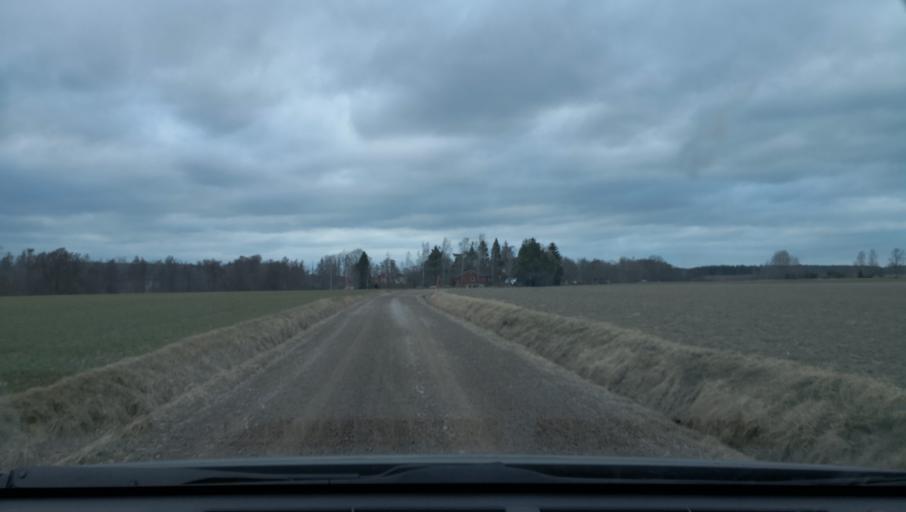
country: SE
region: Vaestmanland
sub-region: Kopings Kommun
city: Kolsva
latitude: 59.5378
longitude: 15.8938
